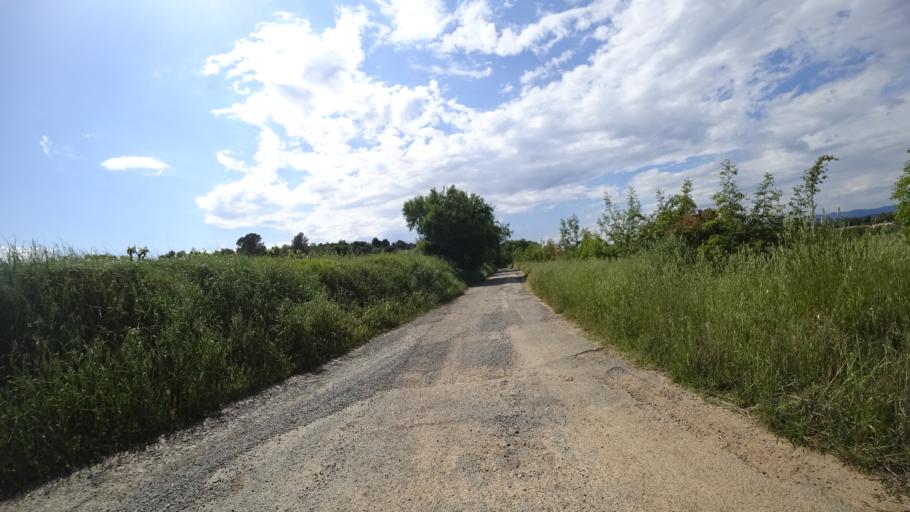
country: FR
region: Languedoc-Roussillon
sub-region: Departement de l'Aude
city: Ginestas
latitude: 43.2633
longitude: 2.8811
